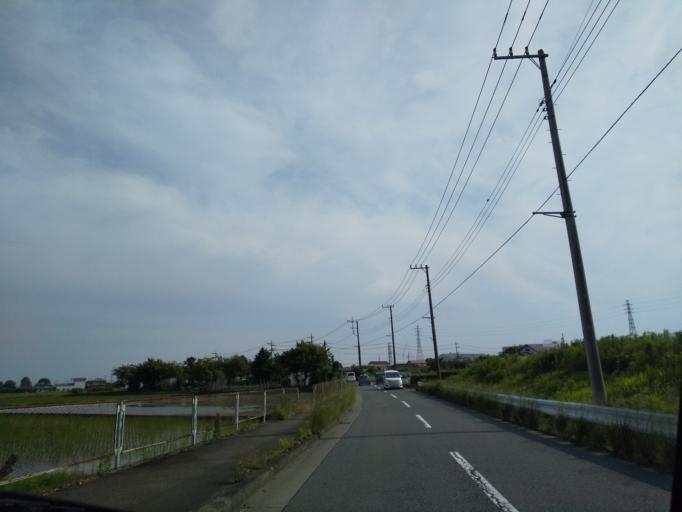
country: JP
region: Kanagawa
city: Zama
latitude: 35.5008
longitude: 139.3509
